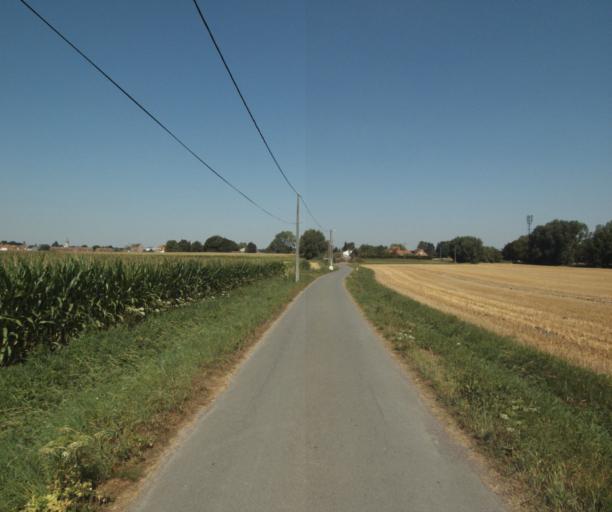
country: FR
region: Nord-Pas-de-Calais
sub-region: Departement du Nord
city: Wervicq-Sud
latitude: 50.7662
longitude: 3.0617
